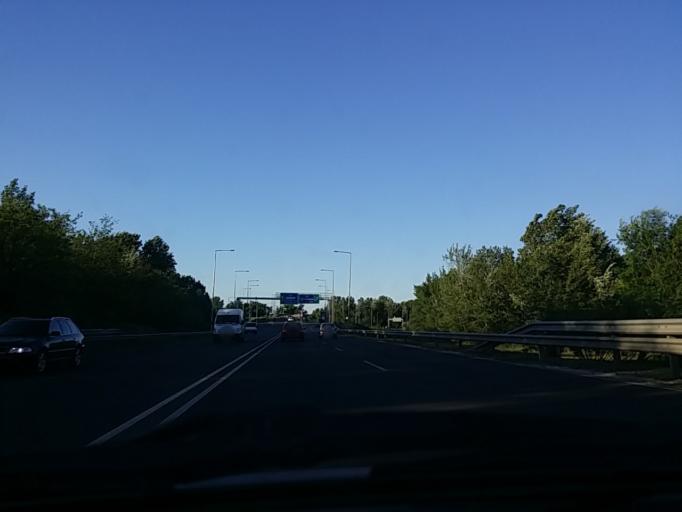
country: HU
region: Budapest
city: Budapest IV. keruelet
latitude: 47.5998
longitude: 19.0998
